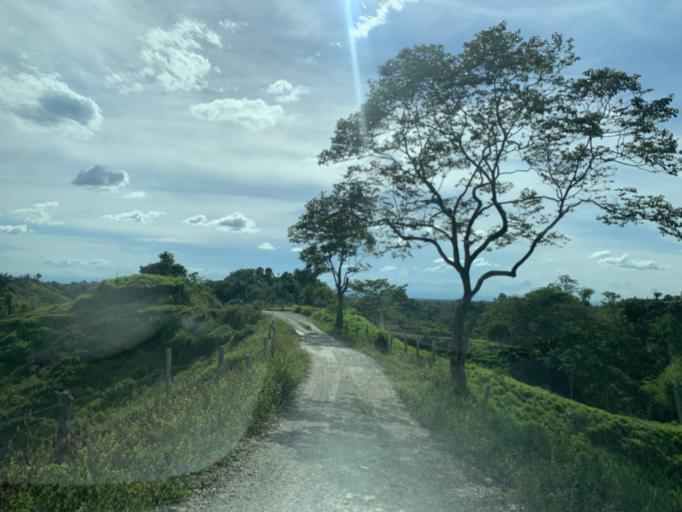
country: CO
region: Boyaca
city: Puerto Boyaca
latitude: 6.0085
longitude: -74.3831
